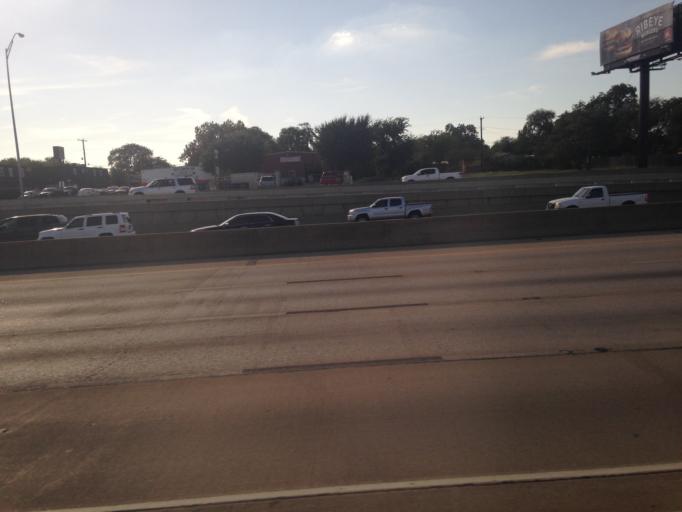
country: US
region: Texas
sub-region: Tarrant County
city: Fort Worth
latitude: 32.7094
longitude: -97.3204
